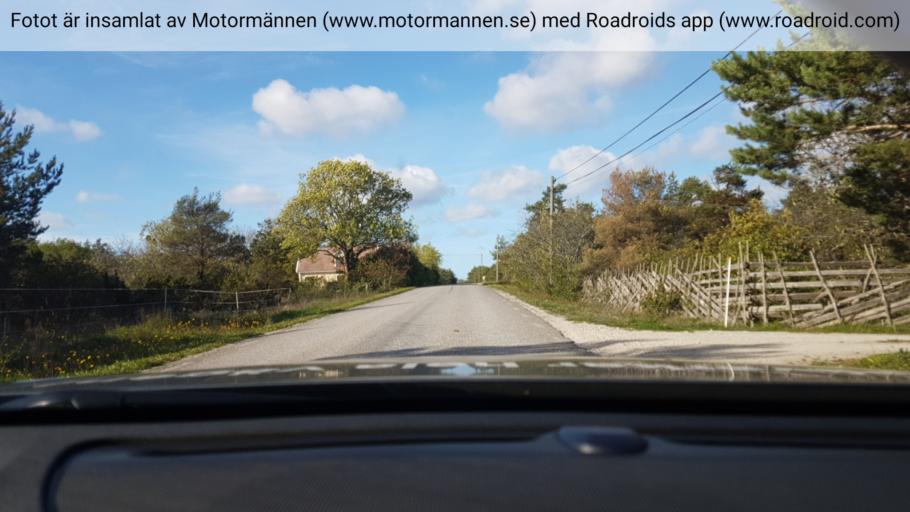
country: SE
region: Gotland
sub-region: Gotland
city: Slite
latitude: 57.8575
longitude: 19.0228
